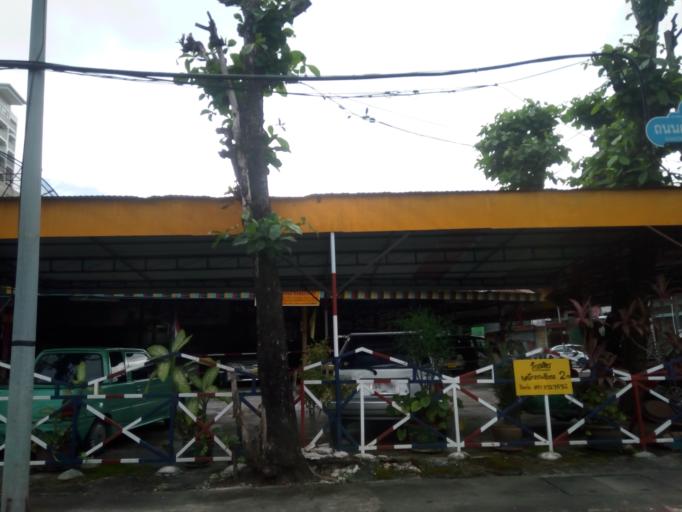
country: TH
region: Phuket
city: Ban Talat Nua
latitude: 7.8727
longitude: 98.3785
